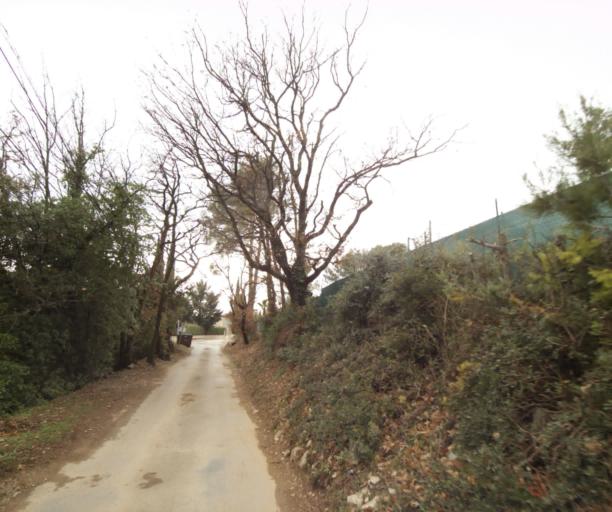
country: FR
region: Provence-Alpes-Cote d'Azur
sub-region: Departement du Var
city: Trans-en-Provence
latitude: 43.5088
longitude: 6.4926
